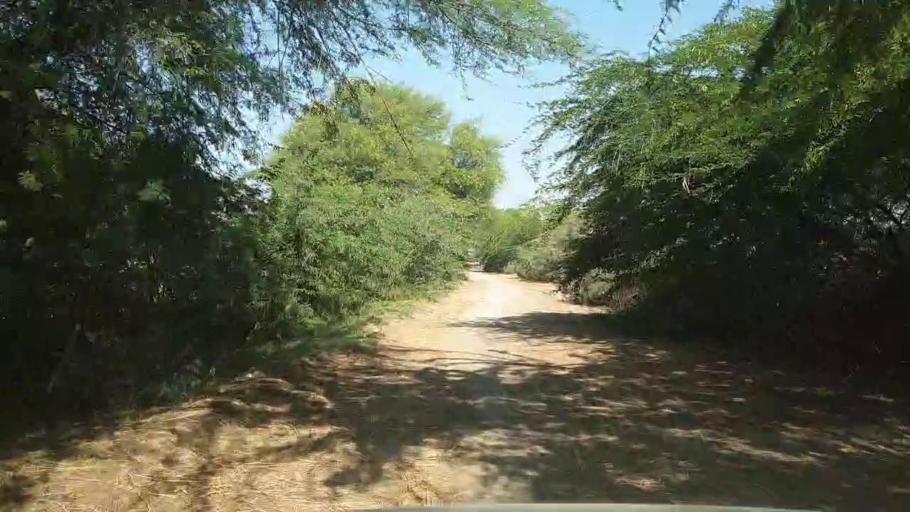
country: PK
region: Sindh
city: Talhar
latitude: 24.8181
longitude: 68.7837
